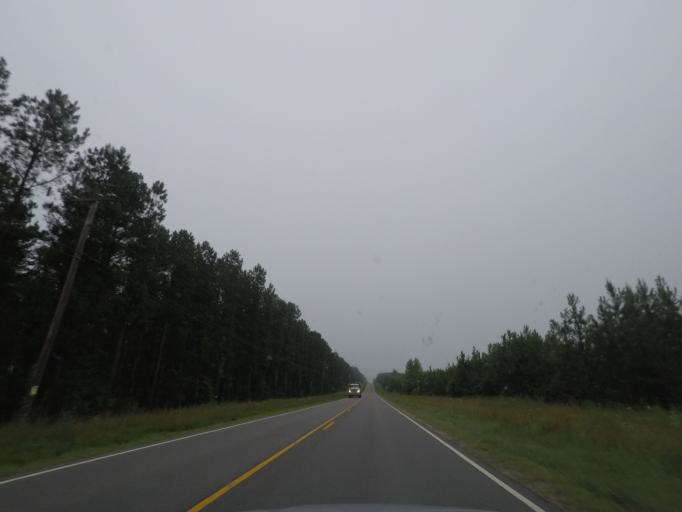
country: US
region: Virginia
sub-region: Buckingham County
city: Buckingham
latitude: 37.5959
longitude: -78.3980
